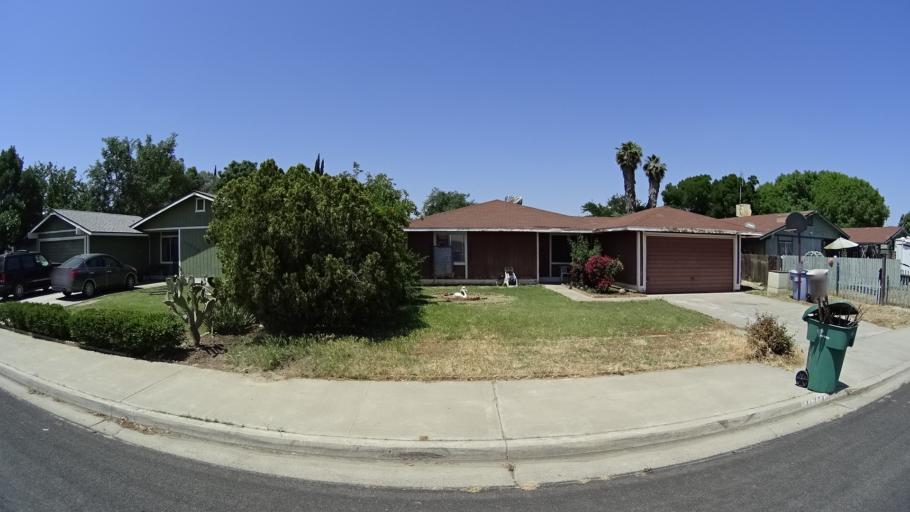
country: US
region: California
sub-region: Kings County
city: Armona
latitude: 36.3090
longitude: -119.7021
